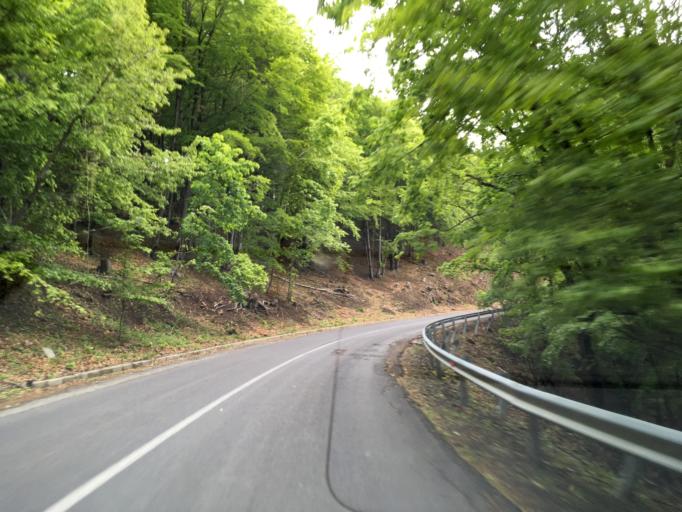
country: HU
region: Nograd
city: Batonyterenye
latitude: 47.9099
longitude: 19.8859
